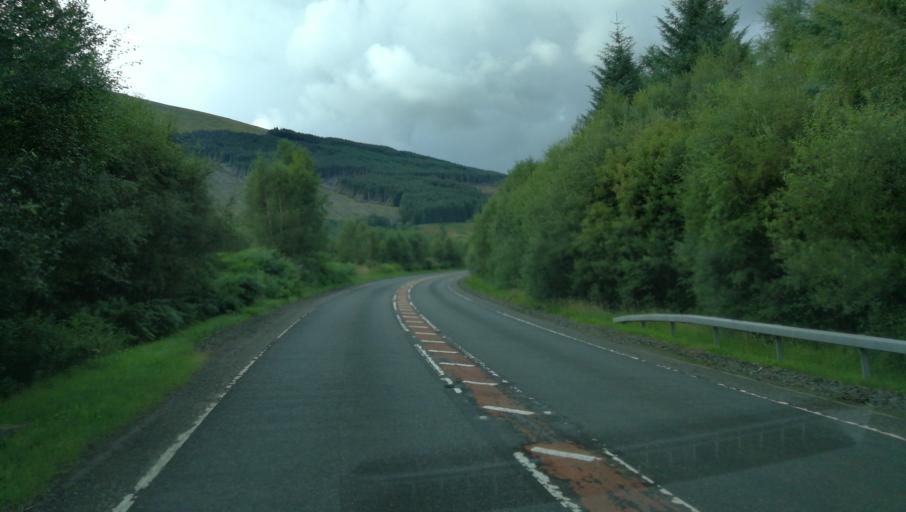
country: GB
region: Scotland
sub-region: Stirling
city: Callander
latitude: 56.3506
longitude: -4.3286
